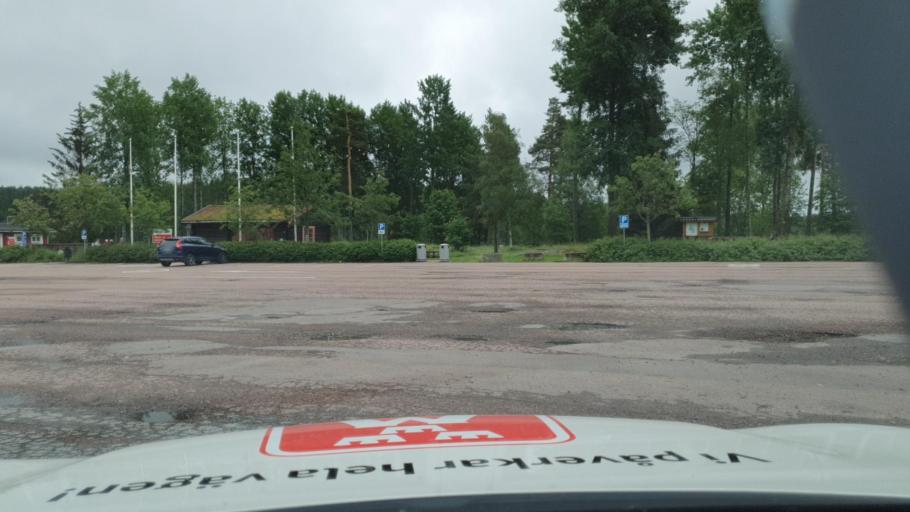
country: SE
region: Vaermland
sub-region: Grums Kommun
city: Grums
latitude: 59.3673
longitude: 13.1408
